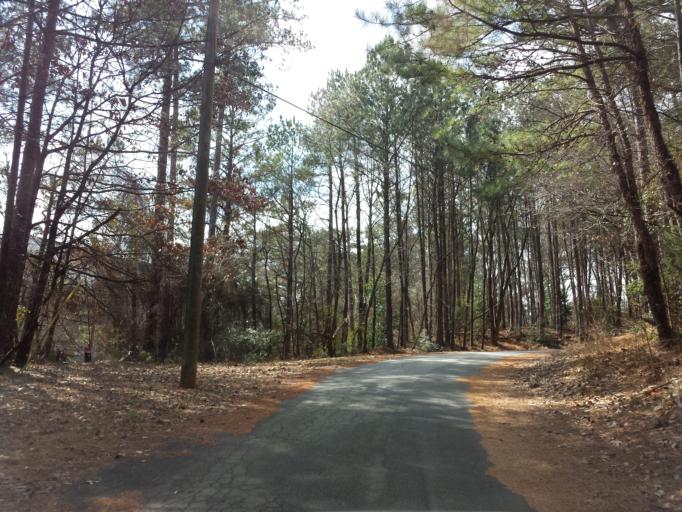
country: US
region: Georgia
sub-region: Cobb County
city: Vinings
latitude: 33.8903
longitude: -84.4508
